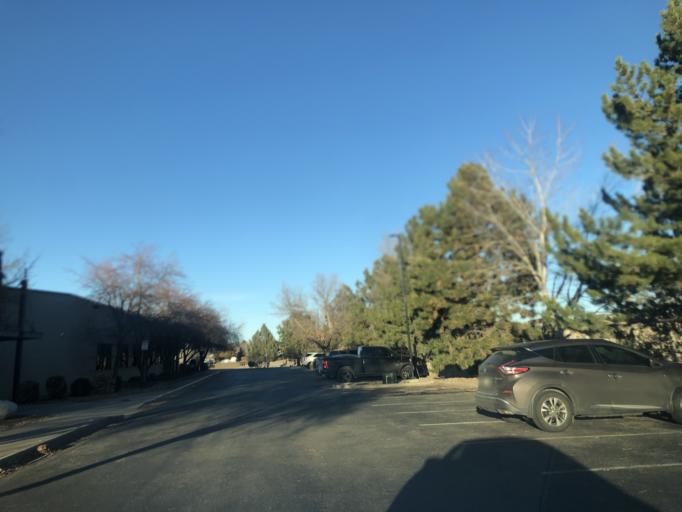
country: US
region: Colorado
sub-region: Adams County
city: Aurora
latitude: 39.7194
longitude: -104.8144
